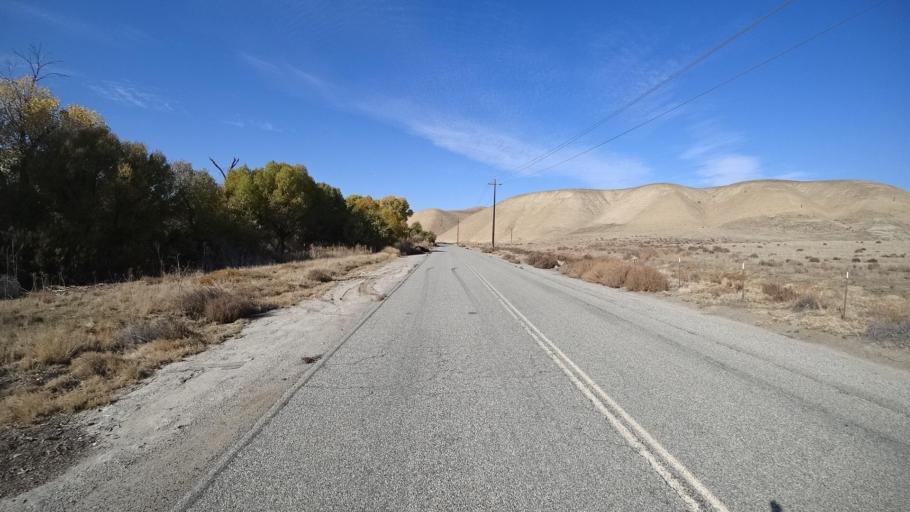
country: US
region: California
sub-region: Kern County
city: Oildale
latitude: 35.5282
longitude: -118.9511
